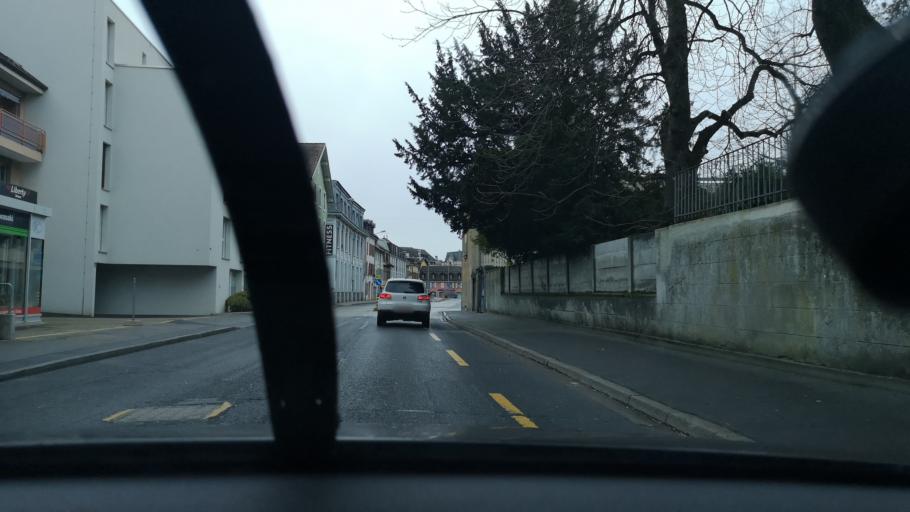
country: CH
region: Vaud
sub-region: Jura-Nord vaudois District
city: Yverdon-les-Bains
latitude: 46.7822
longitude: 6.6355
